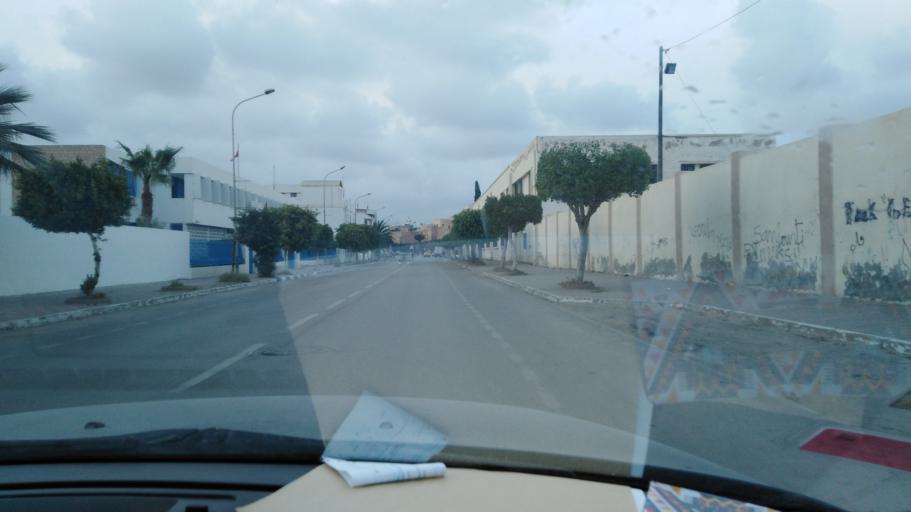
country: TN
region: Safaqis
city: Sfax
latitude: 34.7310
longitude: 10.7586
